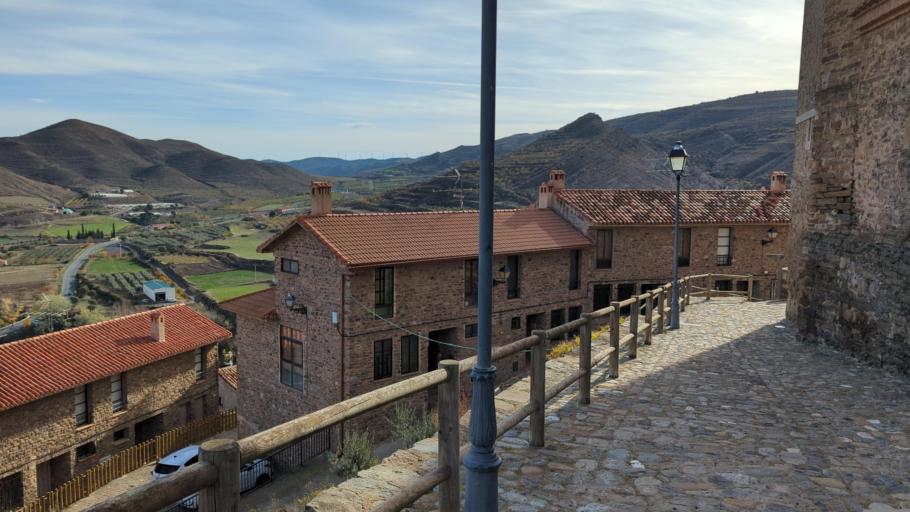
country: ES
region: La Rioja
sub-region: Provincia de La Rioja
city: Cornago
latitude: 42.0658
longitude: -2.0954
